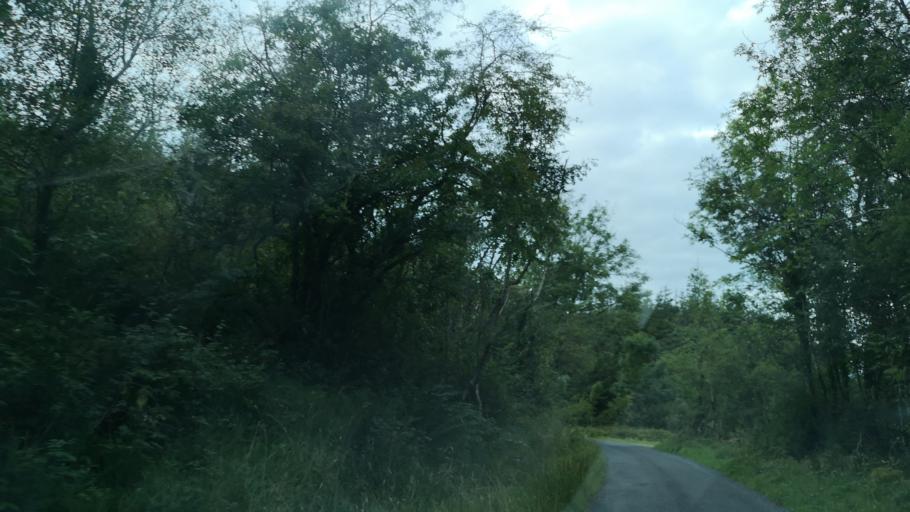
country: IE
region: Connaught
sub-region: County Galway
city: Loughrea
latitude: 53.1372
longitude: -8.5229
